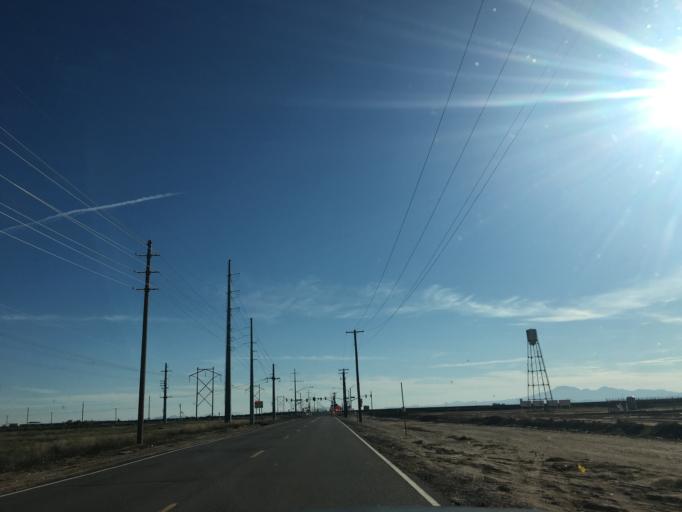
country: US
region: Arizona
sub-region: Pinal County
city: Maricopa
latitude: 33.0274
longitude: -111.9965
